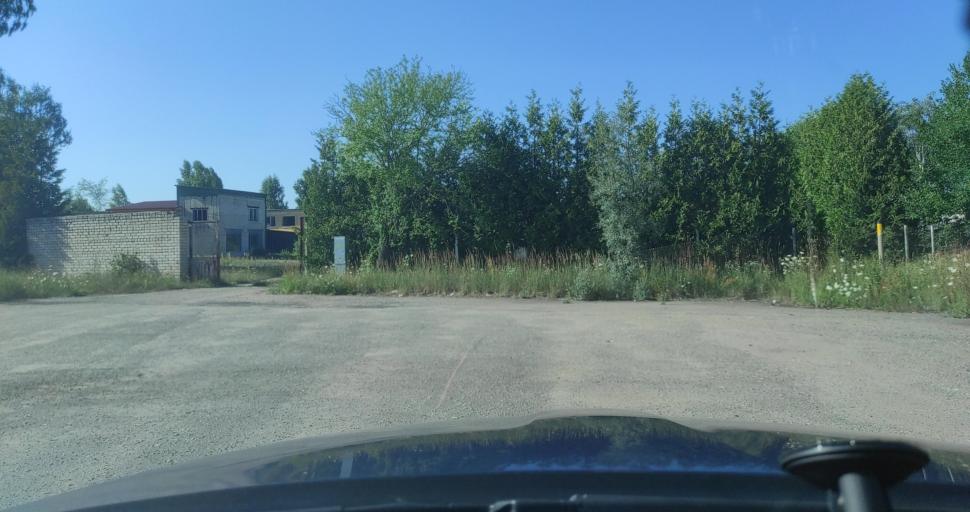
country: LV
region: Skrunda
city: Skrunda
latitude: 56.6776
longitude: 22.0025
